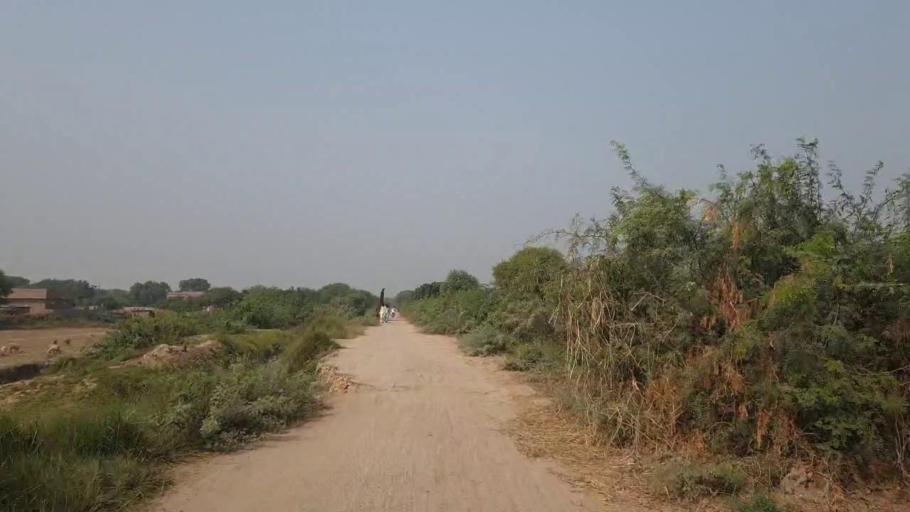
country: PK
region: Sindh
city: Tando Muhammad Khan
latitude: 25.1822
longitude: 68.5980
